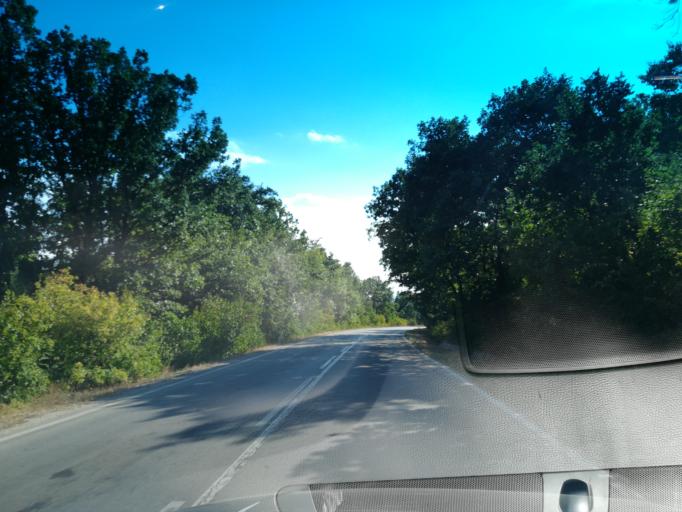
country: BG
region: Khaskovo
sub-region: Obshtina Mineralni Bani
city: Mineralni Bani
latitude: 41.9912
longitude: 25.3582
